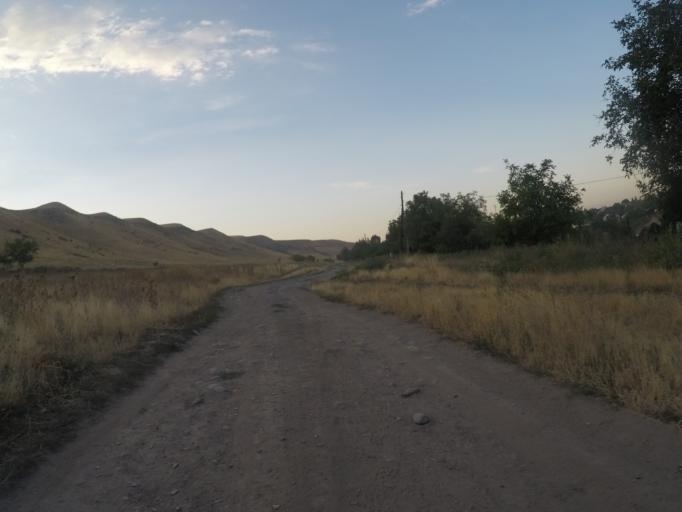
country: KG
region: Chuy
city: Bishkek
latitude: 42.7669
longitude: 74.6385
